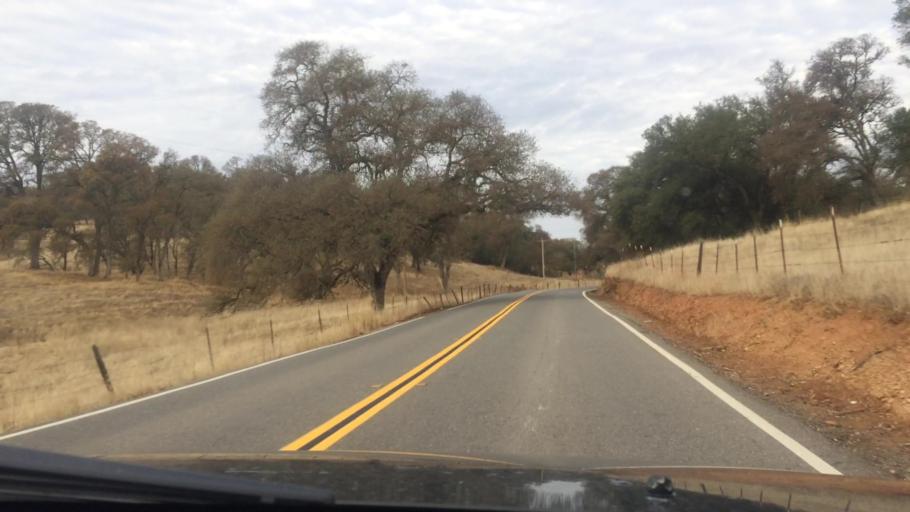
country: US
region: California
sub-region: El Dorado County
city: Cameron Park
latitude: 38.5734
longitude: -120.9953
